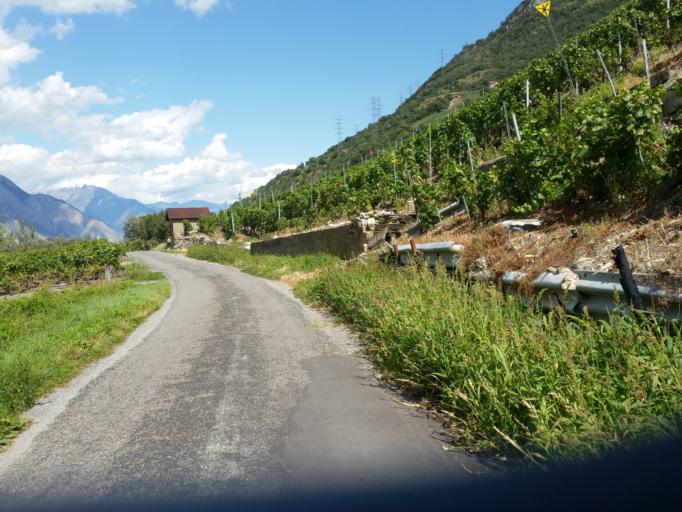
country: CH
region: Valais
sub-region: Martigny District
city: Charrat-les-Chenes
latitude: 46.1310
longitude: 7.1477
